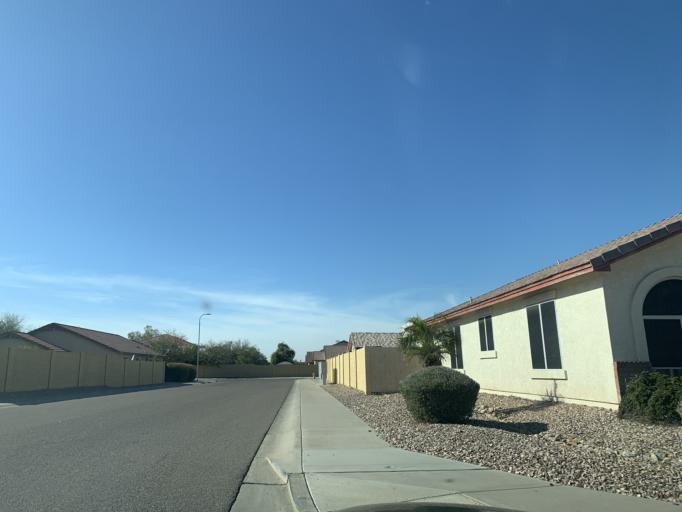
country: US
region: Arizona
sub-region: Maricopa County
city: Laveen
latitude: 33.3985
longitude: -112.1220
